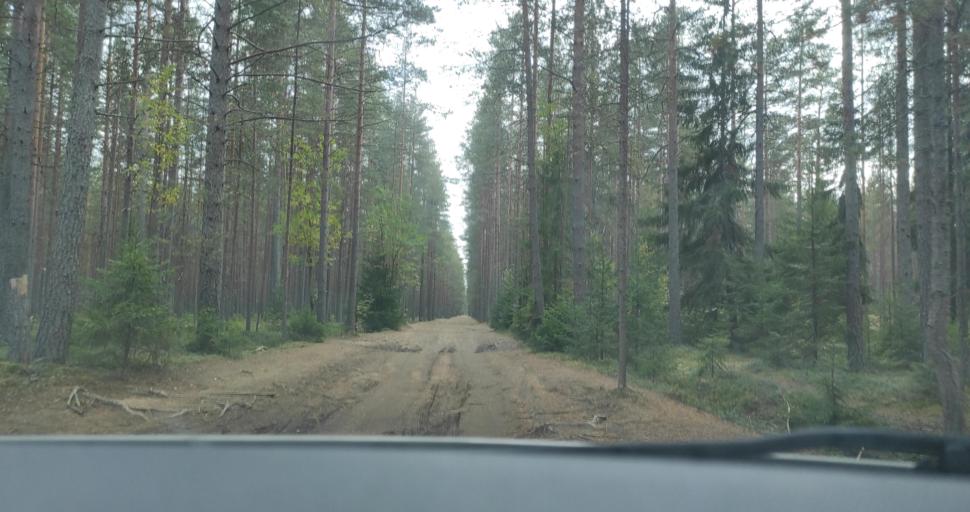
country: RU
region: Leningrad
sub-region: Vsevolzhskij Rajon
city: Vaskelovo
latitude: 60.4115
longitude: 30.3287
